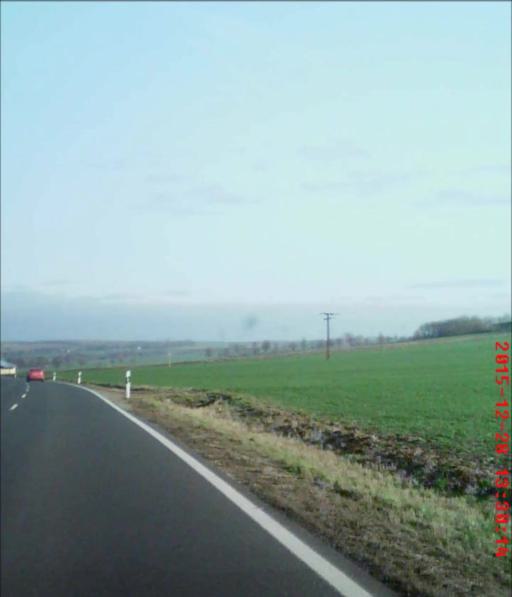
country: DE
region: Thuringia
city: Eberstedt
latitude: 51.0734
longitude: 11.5938
